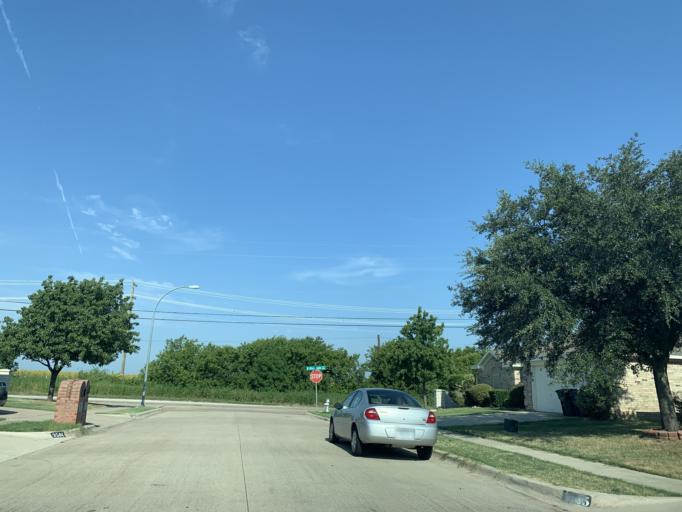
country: US
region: Texas
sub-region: Tarrant County
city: Blue Mound
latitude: 32.8834
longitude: -97.3065
